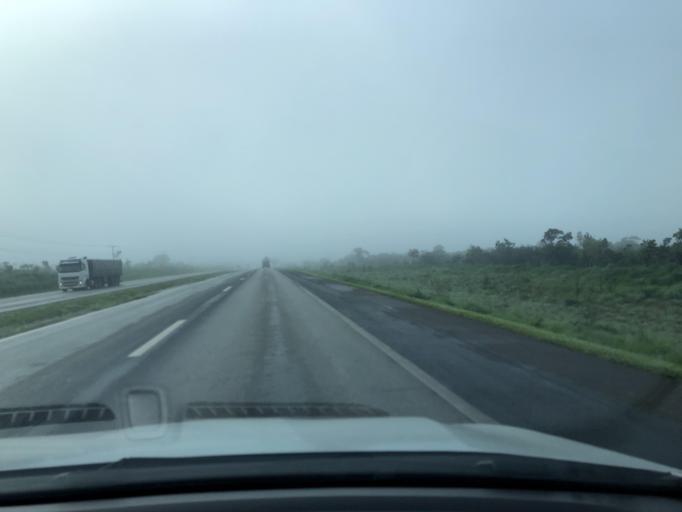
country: BR
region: Goias
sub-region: Luziania
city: Luziania
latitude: -16.2901
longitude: -47.8535
